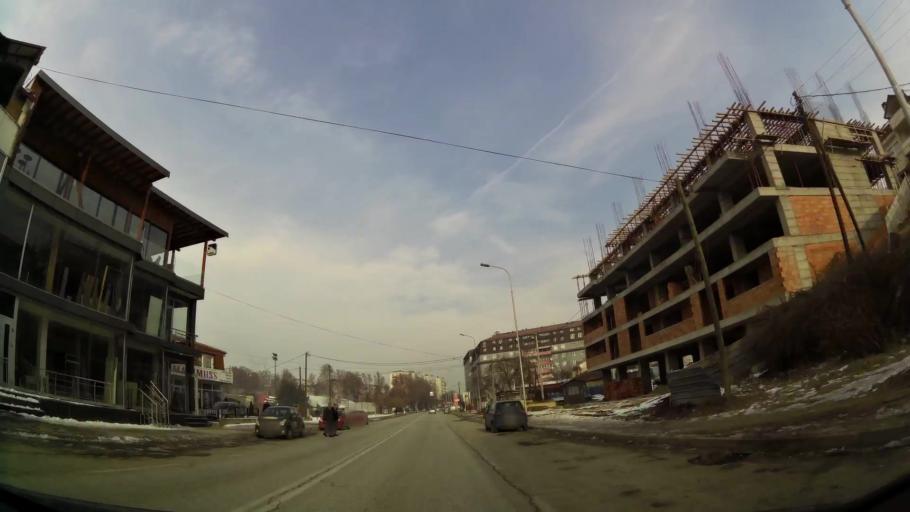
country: MK
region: Cair
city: Cair
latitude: 42.0183
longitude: 21.4355
